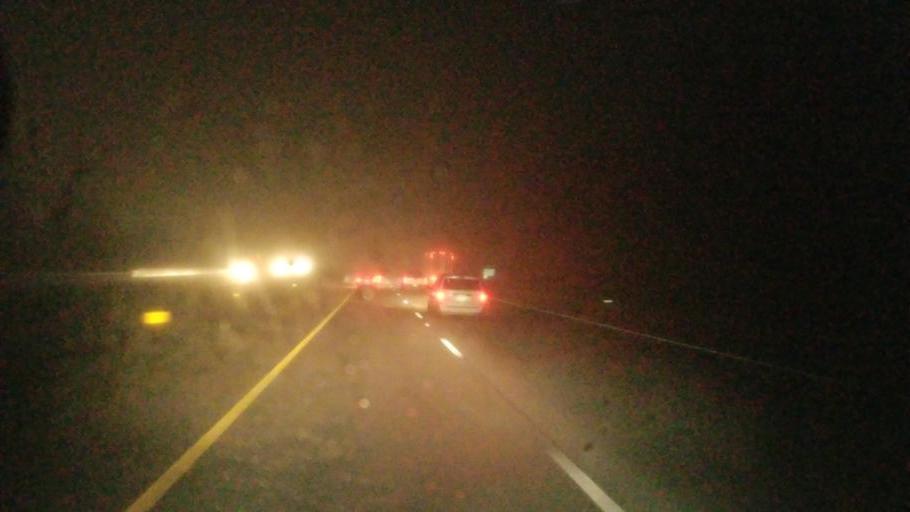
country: US
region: Ohio
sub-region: Pickaway County
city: Circleville
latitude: 39.6071
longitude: -82.9503
